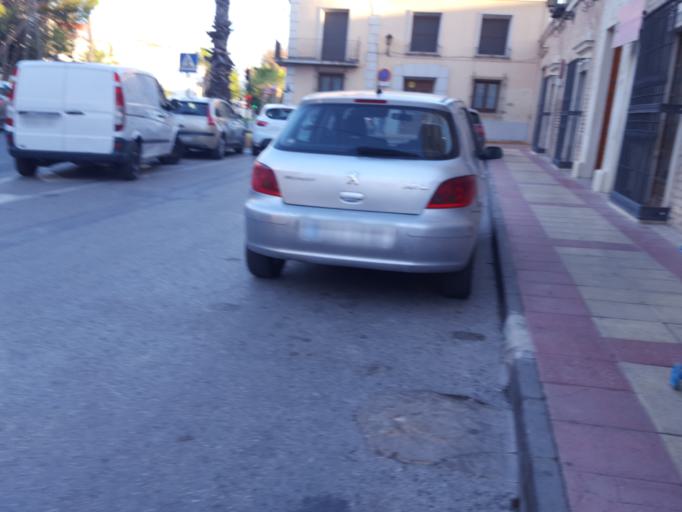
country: ES
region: Murcia
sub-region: Murcia
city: Murcia
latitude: 38.0078
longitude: -1.1512
